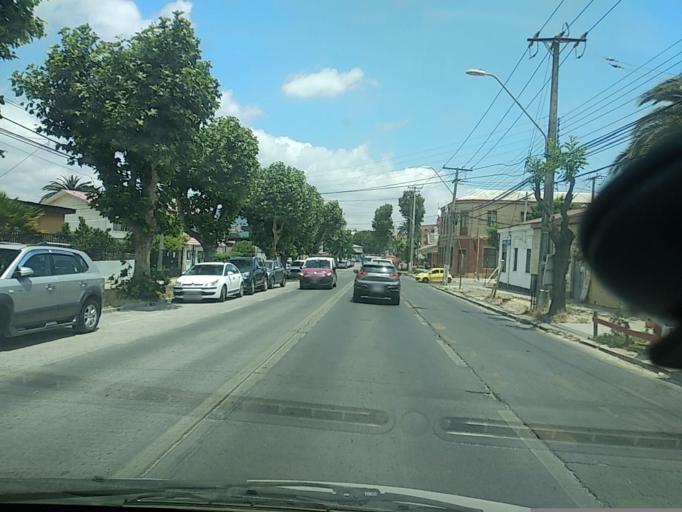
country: CL
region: Valparaiso
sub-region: Provincia de Marga Marga
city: Quilpue
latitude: -33.0442
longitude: -71.4362
